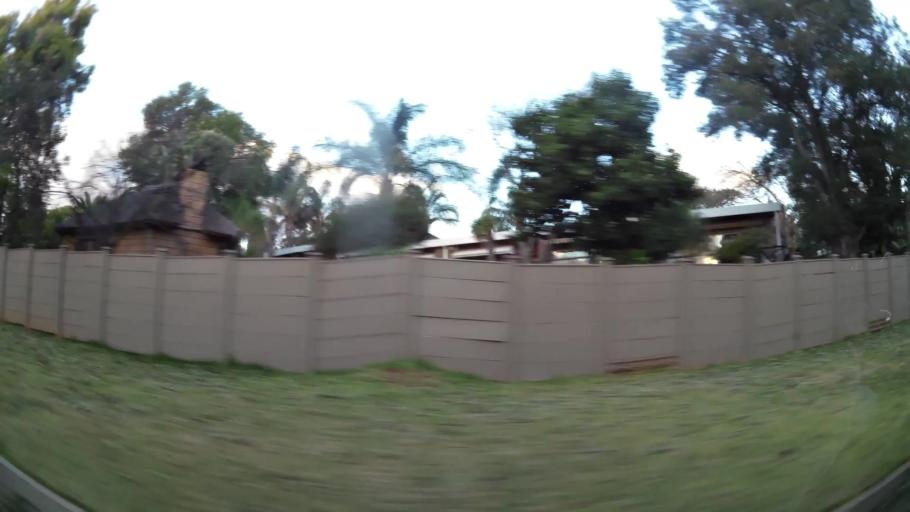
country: ZA
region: Gauteng
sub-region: West Rand District Municipality
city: Krugersdorp
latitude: -26.0738
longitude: 27.7806
